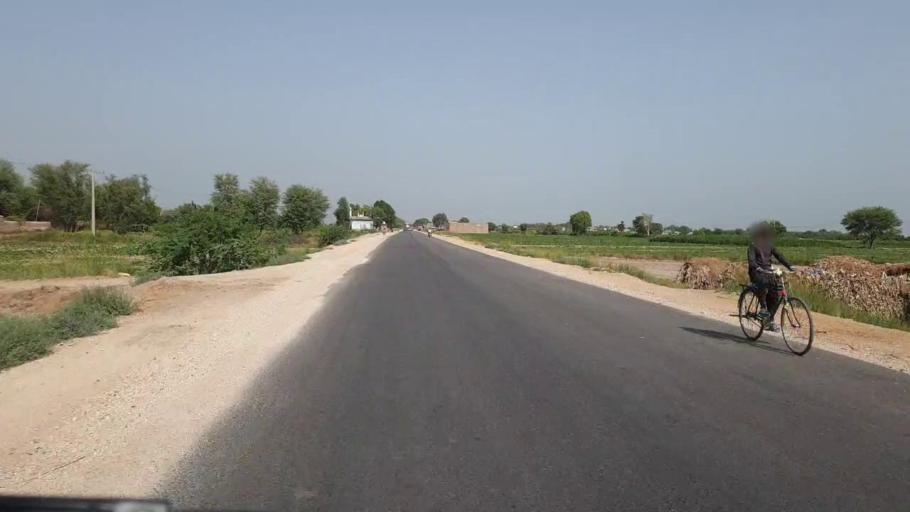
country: PK
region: Sindh
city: Sakrand
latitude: 26.2501
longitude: 68.2094
